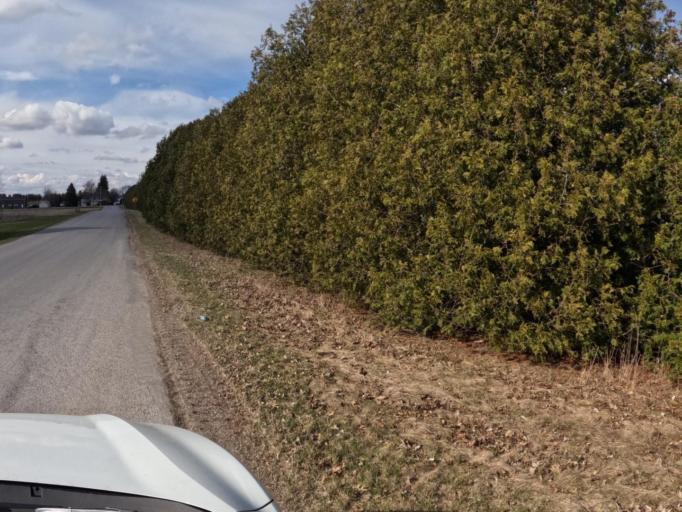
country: CA
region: Ontario
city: Norfolk County
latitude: 42.9000
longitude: -80.2888
